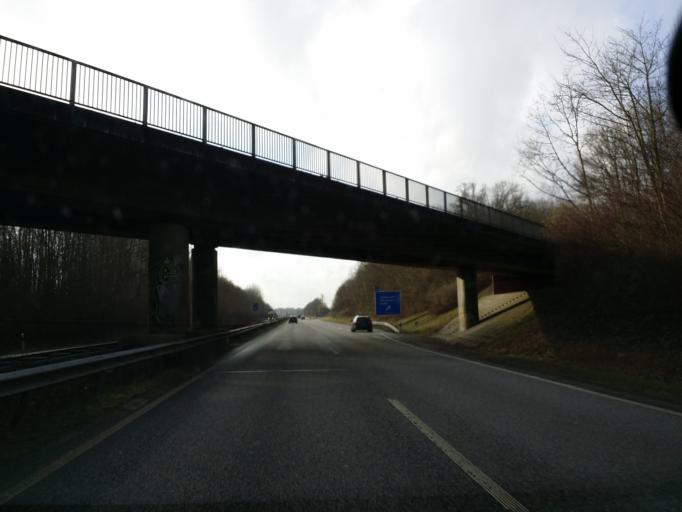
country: DE
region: Schleswig-Holstein
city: Achterwehr
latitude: 54.3196
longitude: 9.9494
